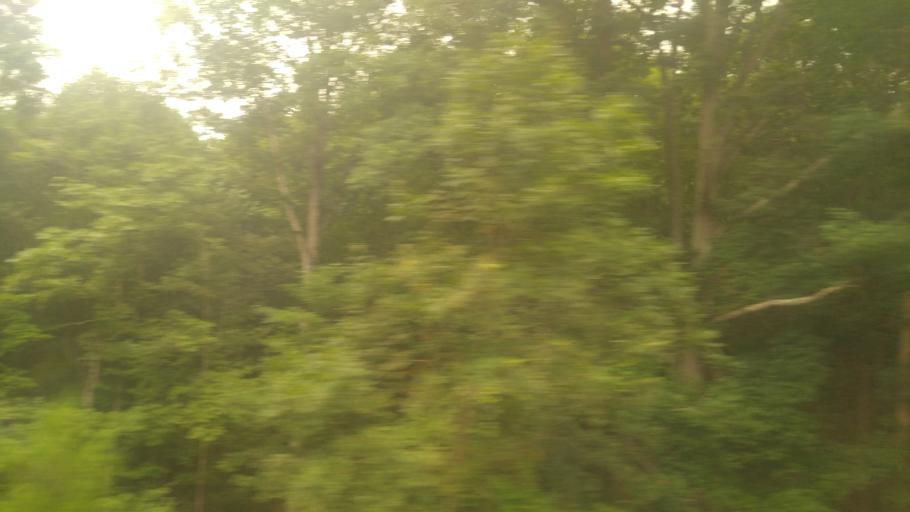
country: US
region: Virginia
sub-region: Henrico County
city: Glen Allen
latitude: 37.7020
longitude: -77.4990
